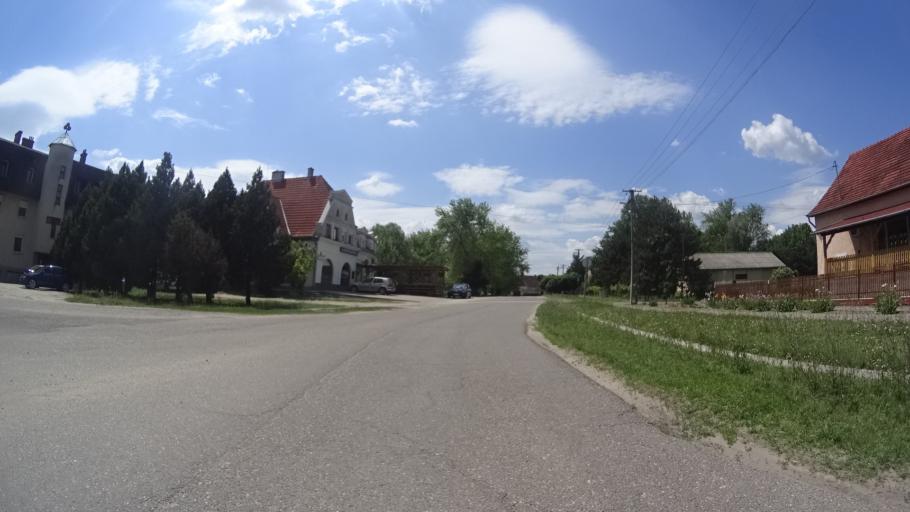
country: HU
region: Bacs-Kiskun
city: Tiszakecske
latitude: 46.9405
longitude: 20.0993
